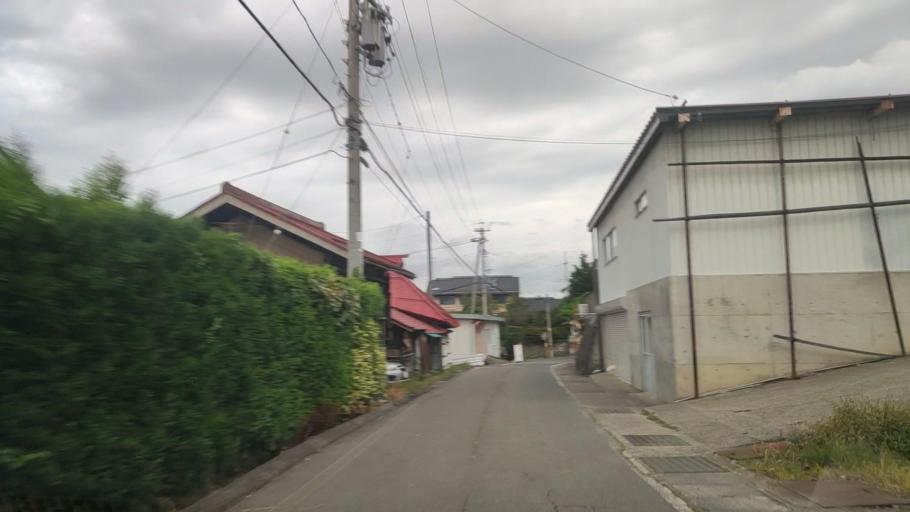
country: JP
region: Nagano
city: Nakano
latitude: 36.7874
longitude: 138.3662
